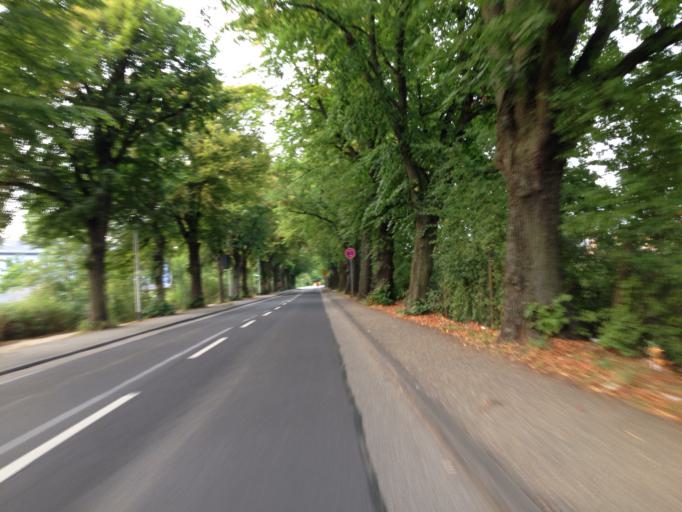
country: DE
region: Hesse
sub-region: Regierungsbezirk Giessen
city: Giessen
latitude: 50.5783
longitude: 8.6590
